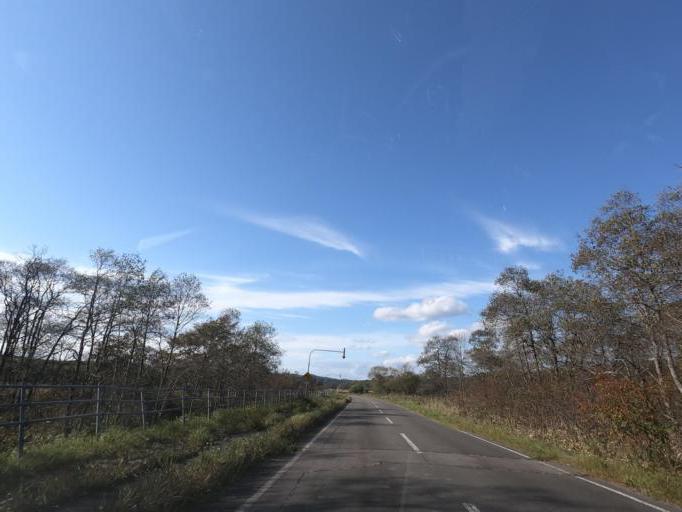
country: JP
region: Hokkaido
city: Obihiro
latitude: 42.6368
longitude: 143.5153
